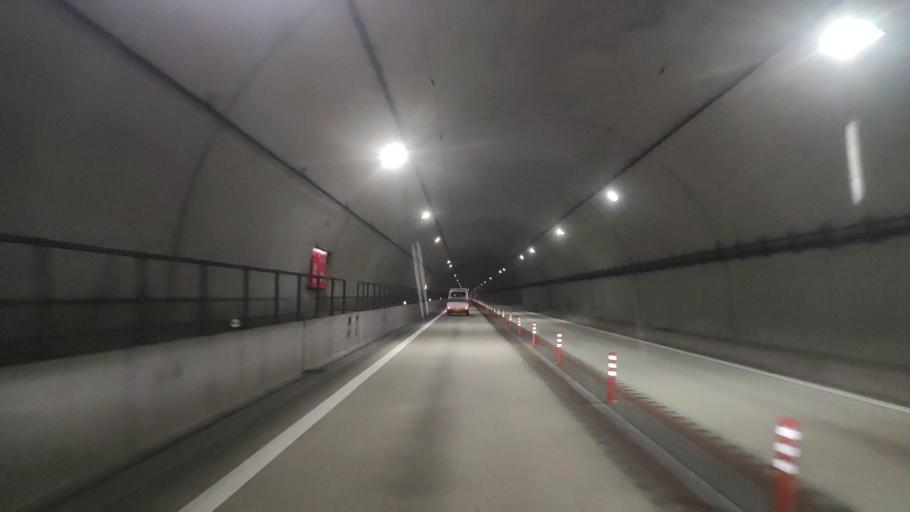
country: JP
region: Wakayama
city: Tanabe
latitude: 33.6009
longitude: 135.4319
